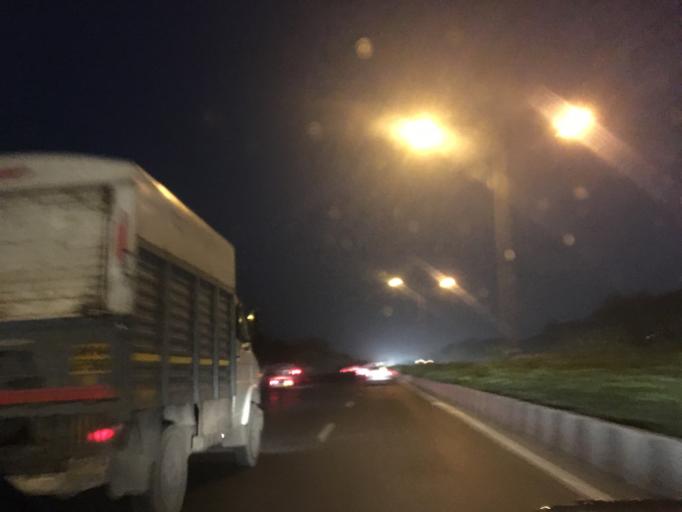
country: IN
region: Maharashtra
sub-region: Mumbai Suburban
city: Powai
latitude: 19.1403
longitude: 72.9479
